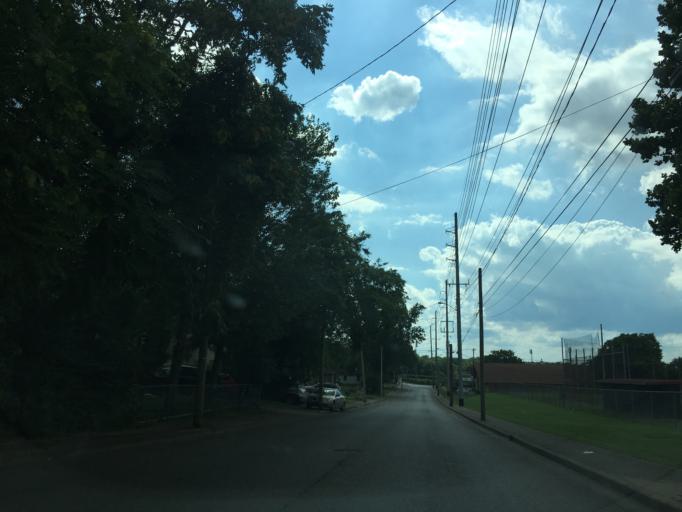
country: US
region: Tennessee
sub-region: Davidson County
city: Nashville
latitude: 36.1622
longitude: -86.8122
